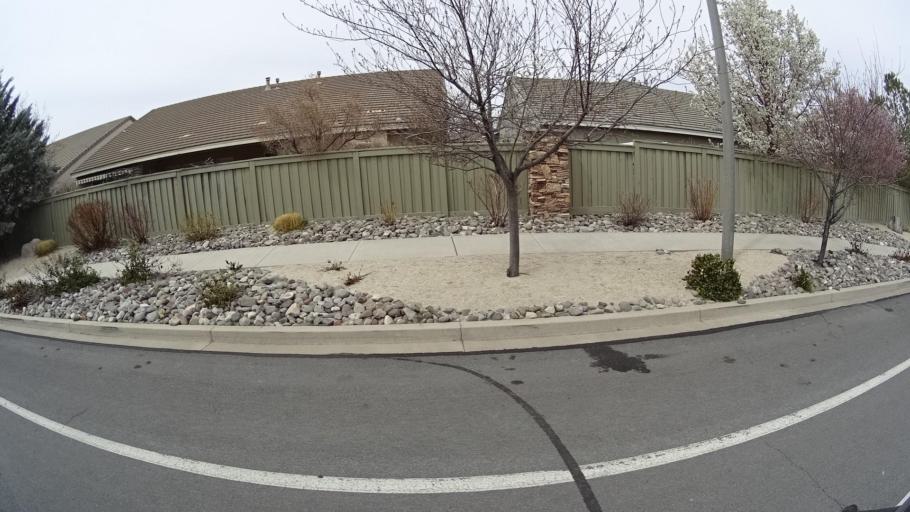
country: US
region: Nevada
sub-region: Washoe County
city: Sparks
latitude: 39.4372
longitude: -119.7373
